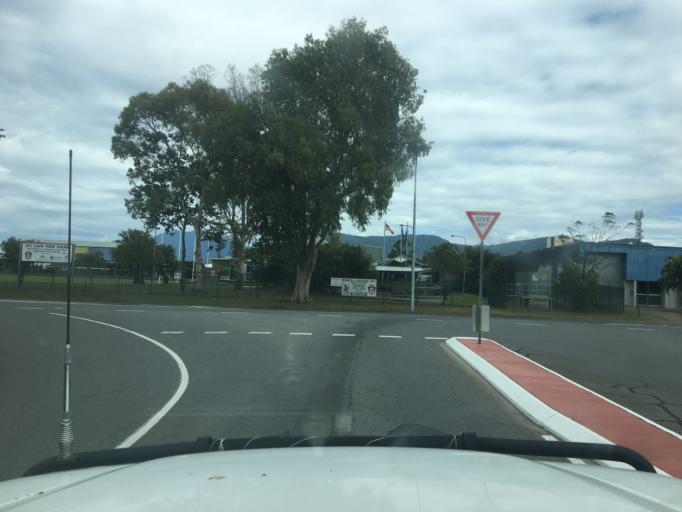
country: AU
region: Queensland
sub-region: Cairns
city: Cairns
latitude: -16.9372
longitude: 145.7680
